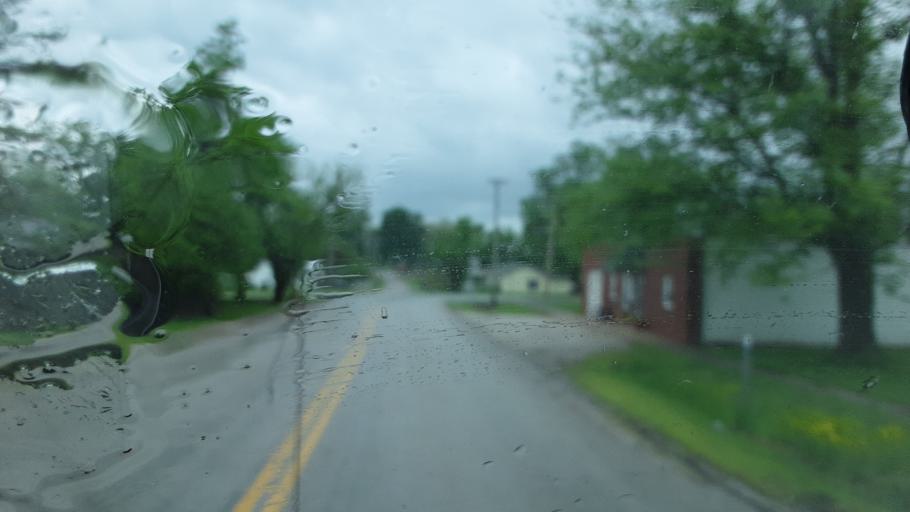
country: US
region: Missouri
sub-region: Monroe County
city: Paris
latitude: 39.4723
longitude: -92.2103
